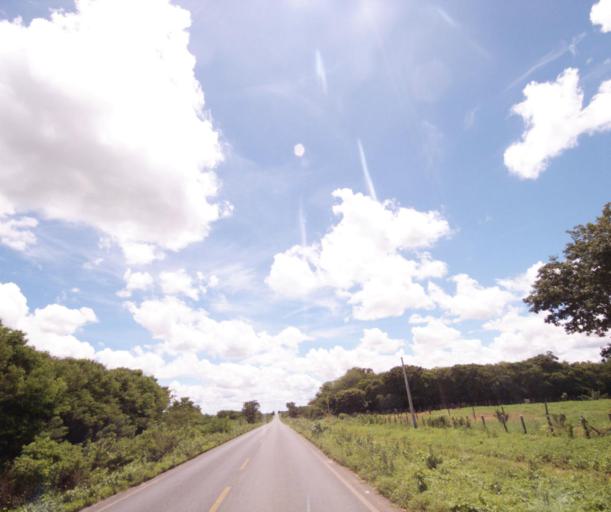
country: BR
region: Bahia
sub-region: Bom Jesus Da Lapa
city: Bom Jesus da Lapa
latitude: -13.2628
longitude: -43.5428
